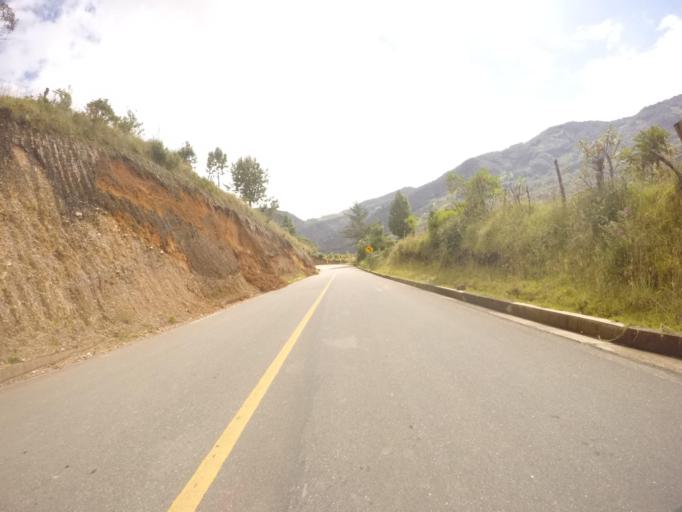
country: CO
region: Cauca
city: Jambalo
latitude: 2.7246
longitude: -76.3235
